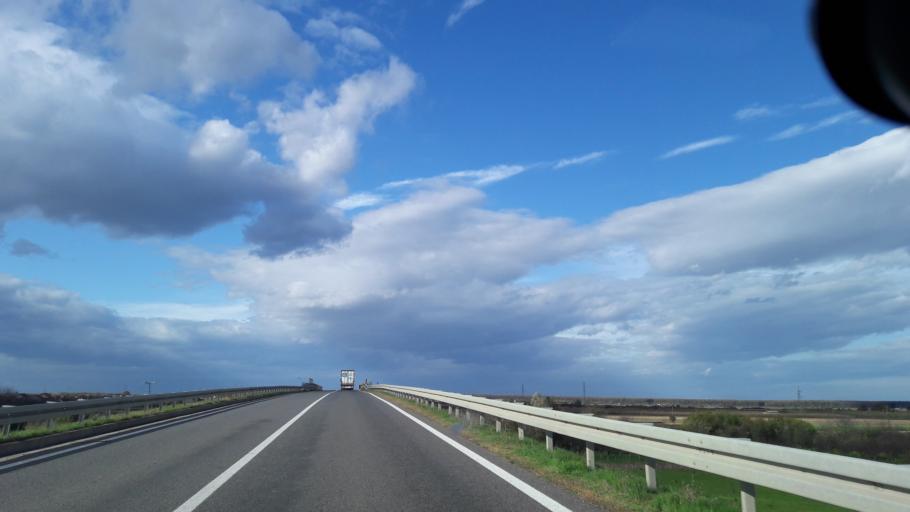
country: HR
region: Osjecko-Baranjska
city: Velimirovac
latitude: 45.4985
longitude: 18.1285
